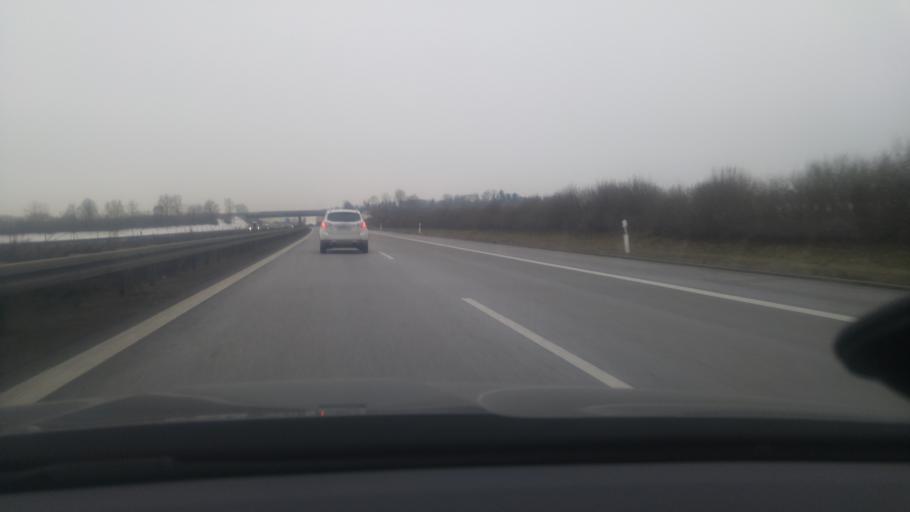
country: DE
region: Baden-Wuerttemberg
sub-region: Regierungsbezirk Stuttgart
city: Bondorf
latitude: 48.5136
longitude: 8.8628
